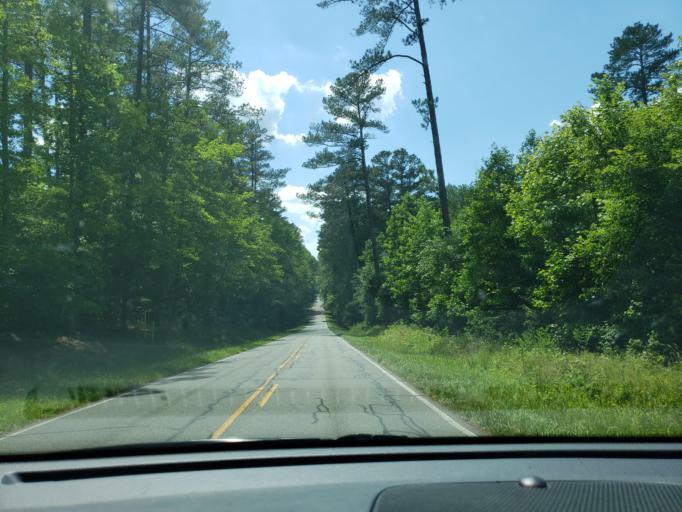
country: US
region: North Carolina
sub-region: Orange County
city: Chapel Hill
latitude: 36.0018
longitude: -79.0354
